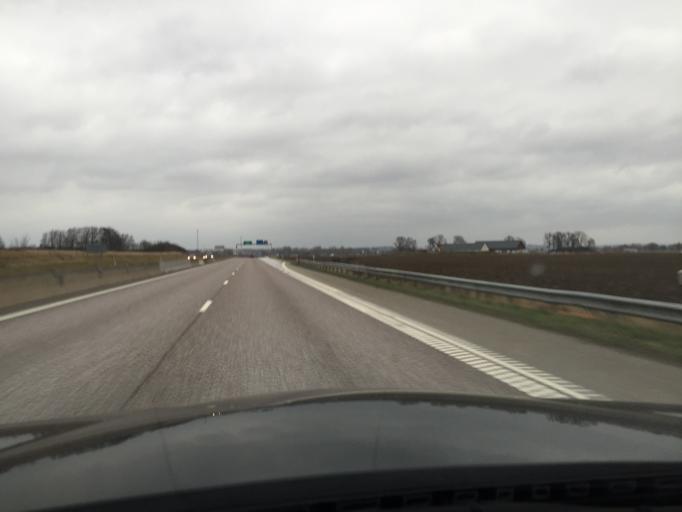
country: SE
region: Skane
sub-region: Lunds Kommun
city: Lund
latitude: 55.6743
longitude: 13.1753
